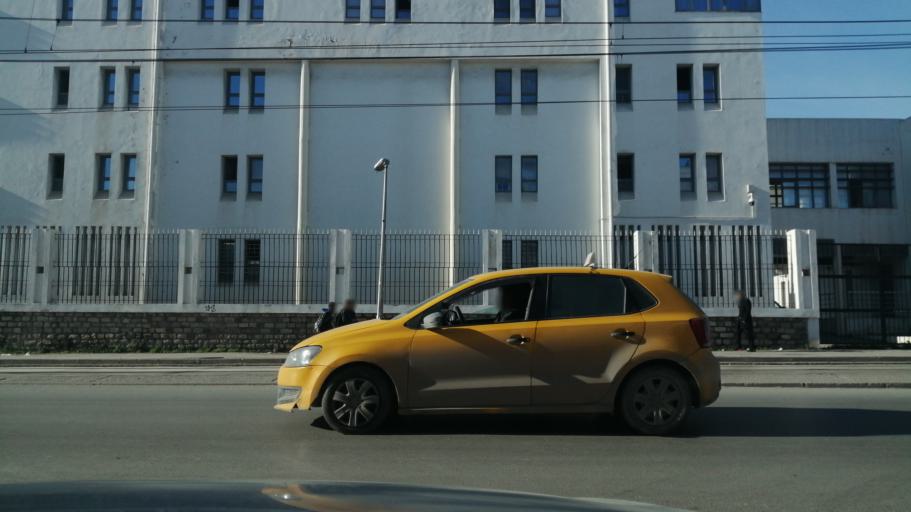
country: TN
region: Tunis
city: Tunis
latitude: 36.8123
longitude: 10.1704
